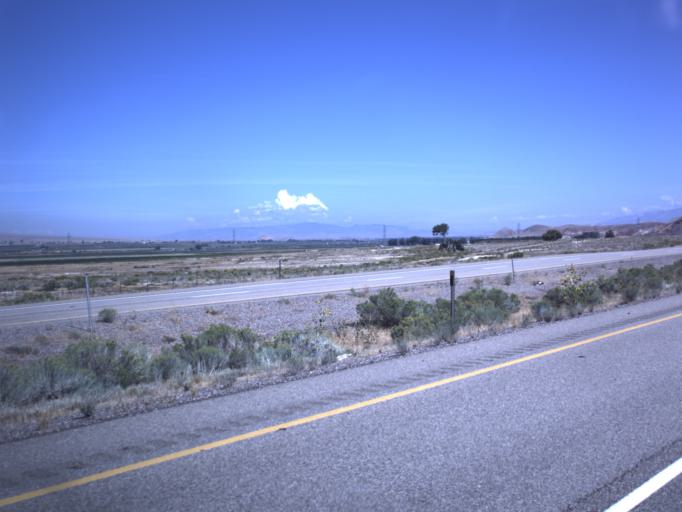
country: US
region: Utah
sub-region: Sevier County
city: Aurora
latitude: 38.8852
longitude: -111.9179
